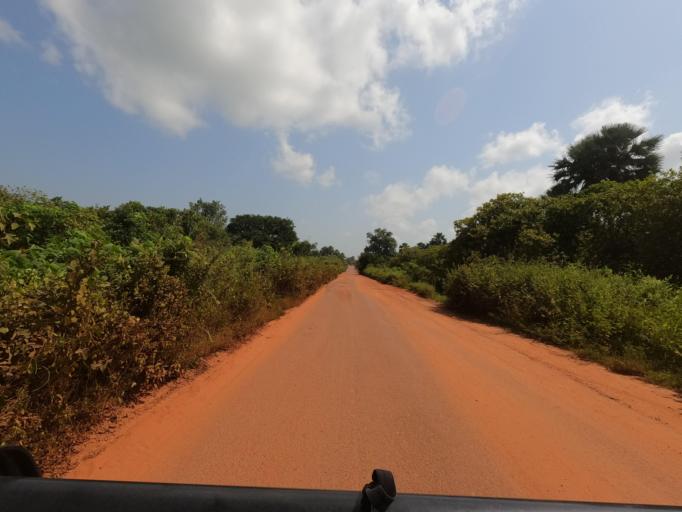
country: GW
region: Cacheu
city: Canchungo
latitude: 12.2861
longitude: -15.7789
